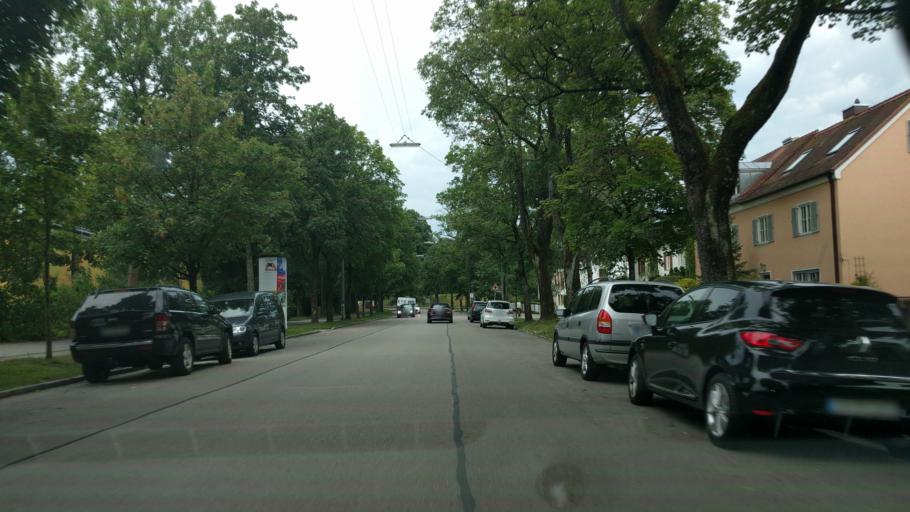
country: DE
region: Bavaria
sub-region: Upper Bavaria
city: Munich
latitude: 48.0995
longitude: 11.5714
